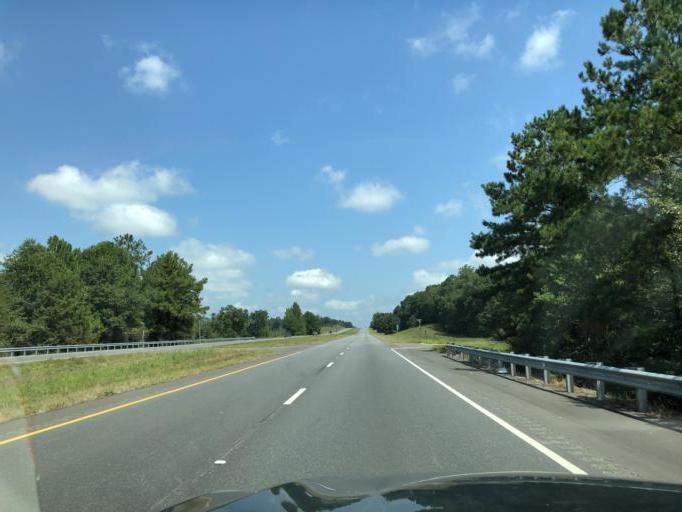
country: US
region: Alabama
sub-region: Henry County
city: Abbeville
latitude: 31.4698
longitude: -85.3042
